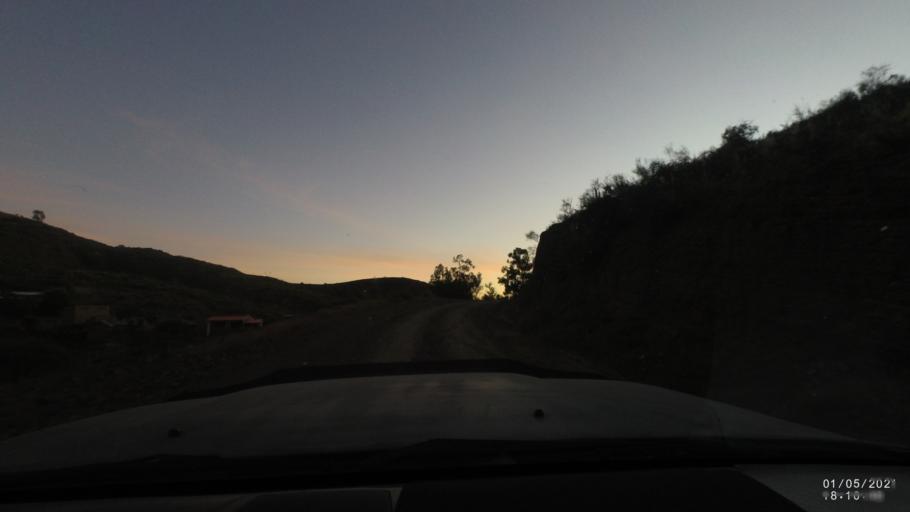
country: BO
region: Cochabamba
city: Capinota
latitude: -17.6841
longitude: -66.1971
